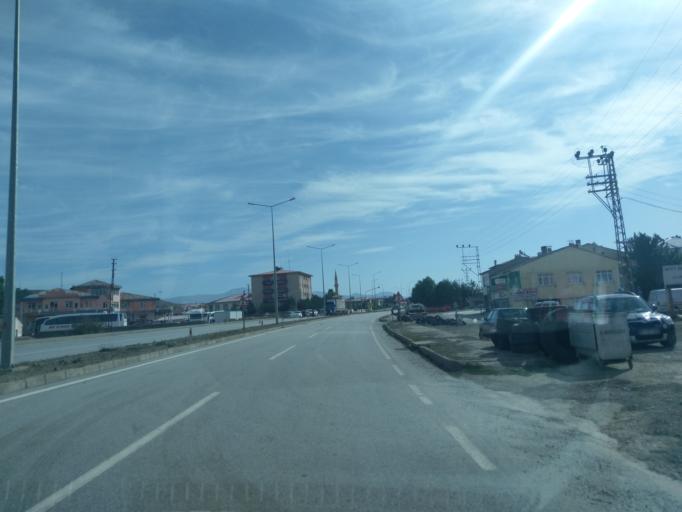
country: TR
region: Sivas
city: Imranli
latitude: 39.8716
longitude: 38.1078
